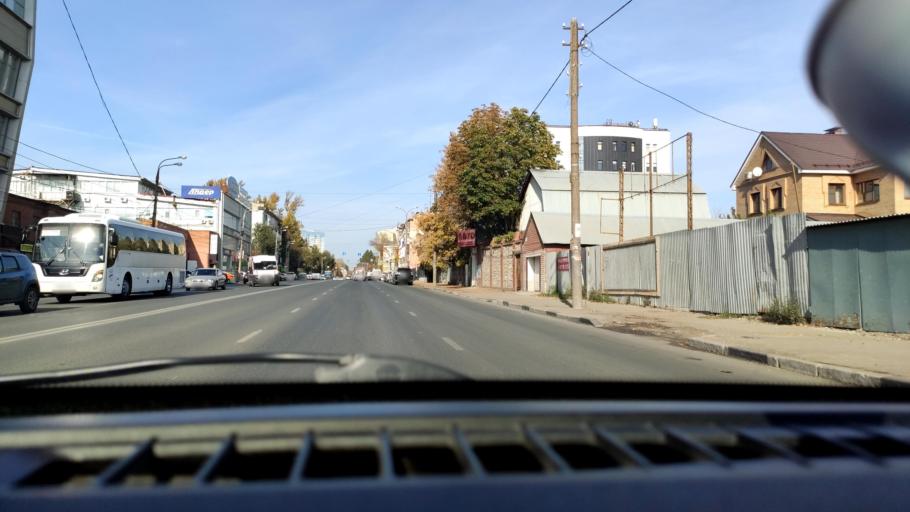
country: RU
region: Samara
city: Samara
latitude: 53.1982
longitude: 50.1905
